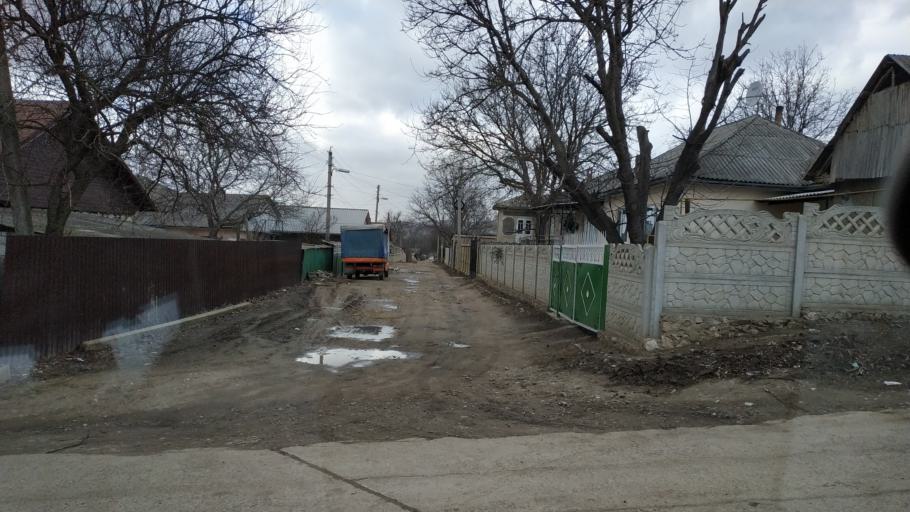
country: MD
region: Calarasi
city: Calarasi
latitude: 47.2772
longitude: 28.2162
